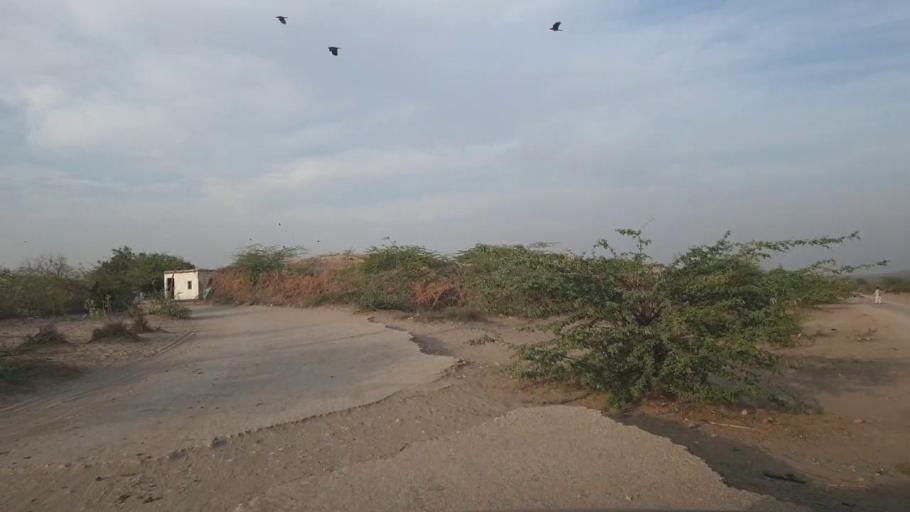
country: PK
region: Sindh
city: Nabisar
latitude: 25.1522
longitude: 69.6804
